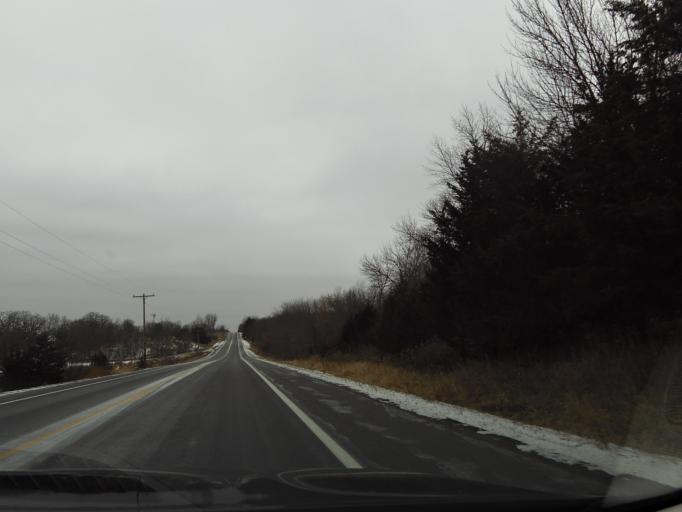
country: US
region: Minnesota
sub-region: Hennepin County
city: Medina
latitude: 45.0223
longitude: -93.6066
